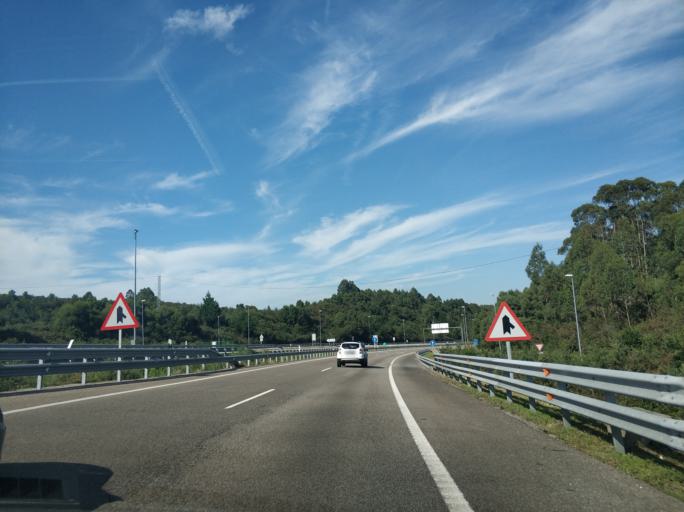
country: ES
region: Asturias
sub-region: Province of Asturias
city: Soto del Barco
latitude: 43.5414
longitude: -6.0407
